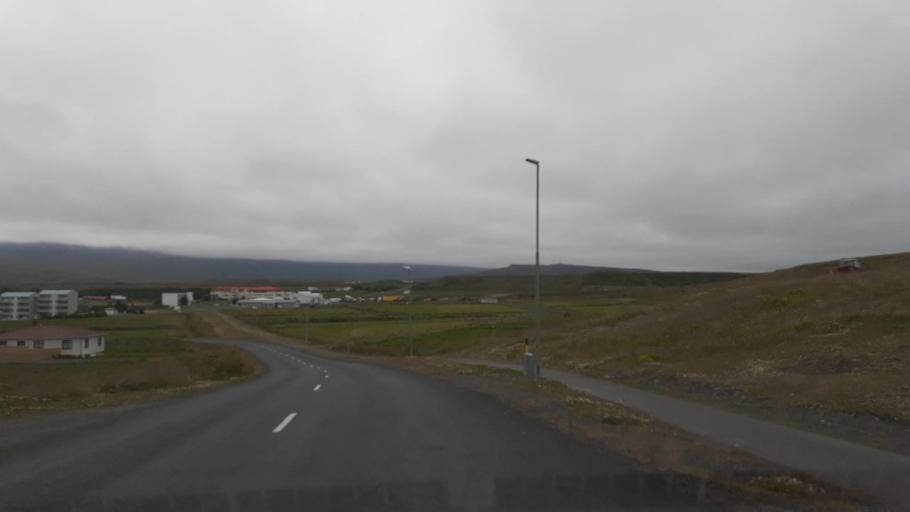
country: IS
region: Northwest
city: Saudarkrokur
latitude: 65.6568
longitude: -20.2972
